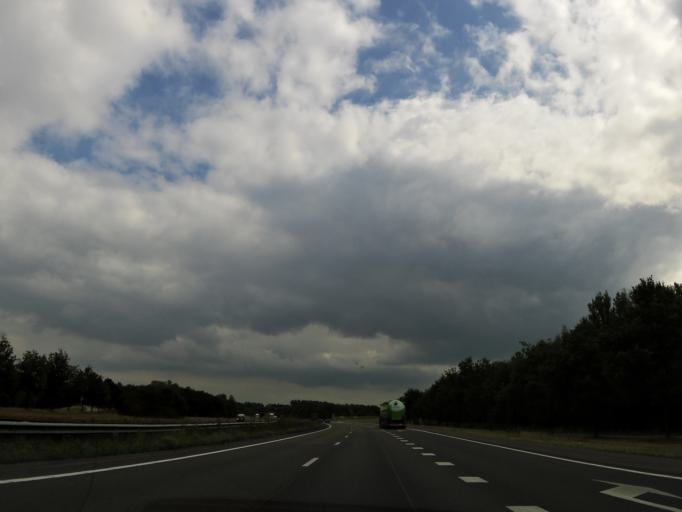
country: NL
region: Limburg
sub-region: Gemeente Weert
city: Weert
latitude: 51.2789
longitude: 5.6569
